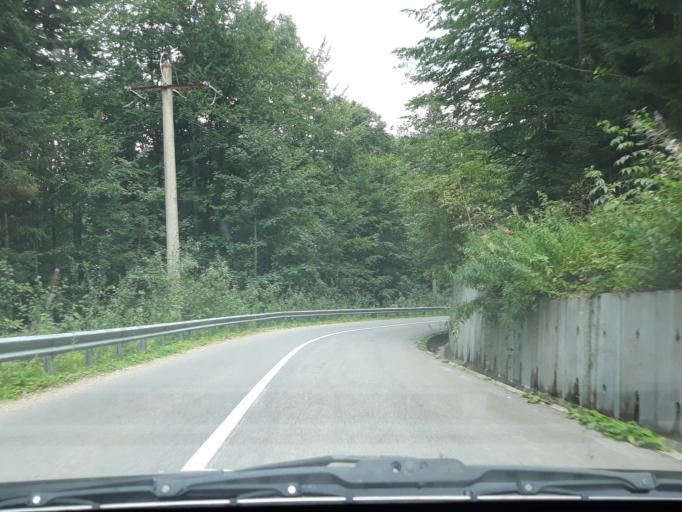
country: RO
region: Bihor
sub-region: Comuna Pietroasa
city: Pietroasa
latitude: 46.5900
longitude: 22.6720
